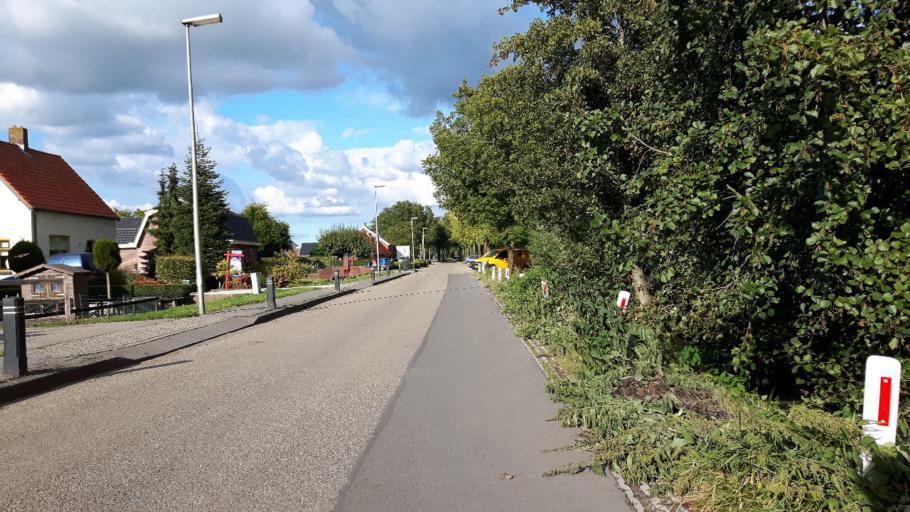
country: NL
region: Utrecht
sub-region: Gemeente Vianen
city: Vianen
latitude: 51.9471
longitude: 5.0719
